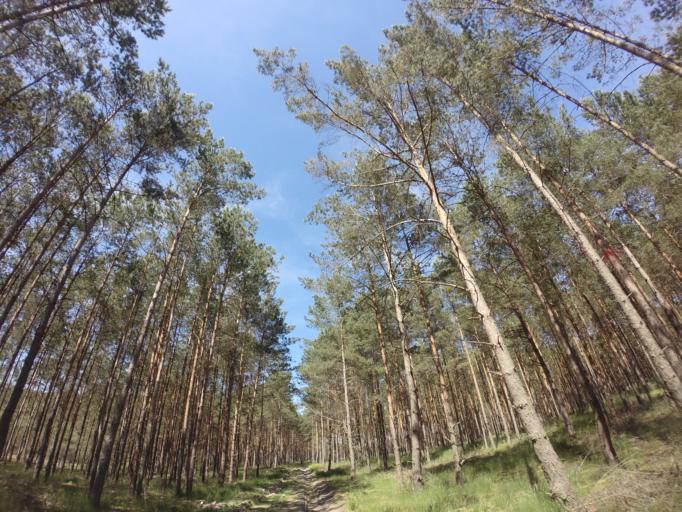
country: PL
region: West Pomeranian Voivodeship
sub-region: Powiat choszczenski
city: Drawno
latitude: 53.1327
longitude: 15.7894
